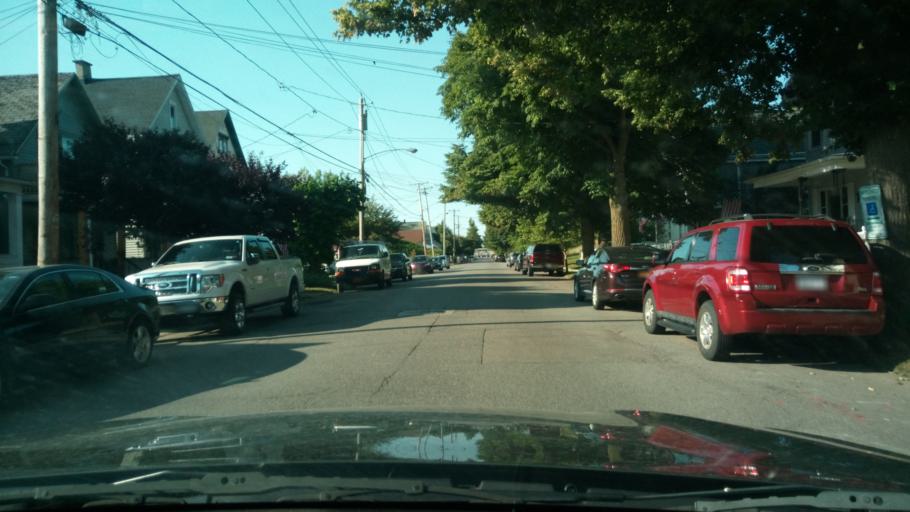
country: US
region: New York
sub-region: Erie County
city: Buffalo
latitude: 42.8677
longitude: -78.8593
